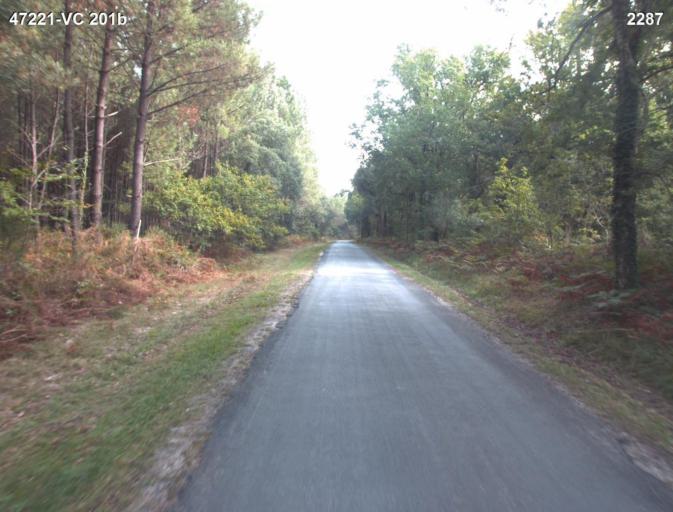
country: FR
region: Aquitaine
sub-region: Departement du Lot-et-Garonne
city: Mezin
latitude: 44.0838
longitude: 0.2251
